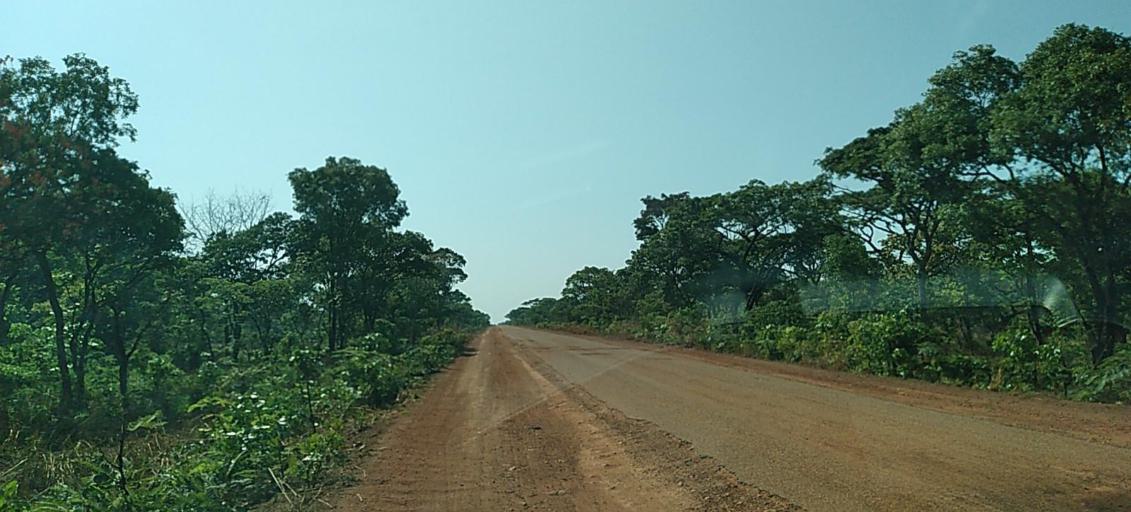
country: ZM
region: North-Western
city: Mwinilunga
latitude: -11.9076
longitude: 25.2918
